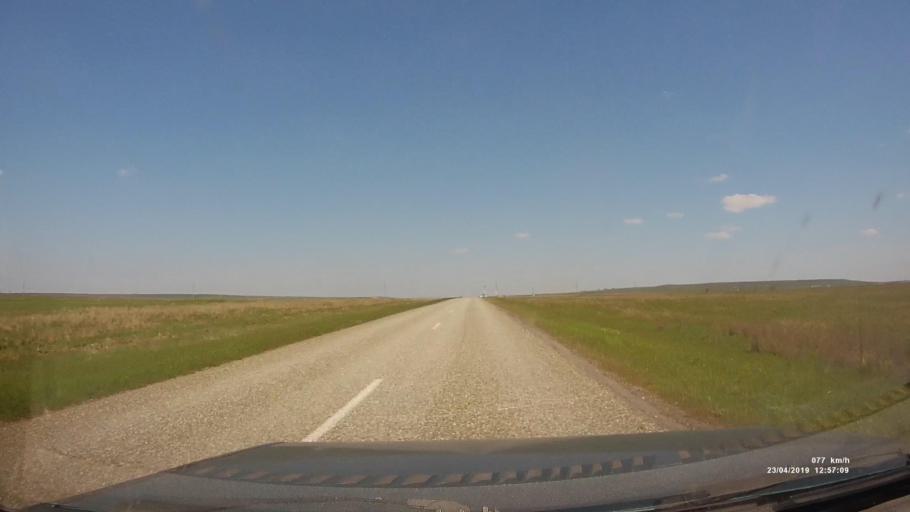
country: RU
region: Kalmykiya
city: Yashalta
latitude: 46.6012
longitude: 42.5787
